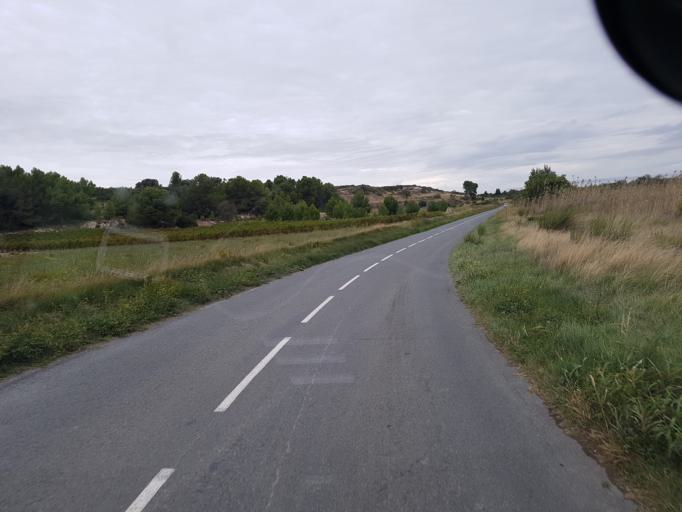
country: FR
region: Languedoc-Roussillon
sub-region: Departement de l'Aude
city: Narbonne
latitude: 43.1392
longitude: 2.9796
